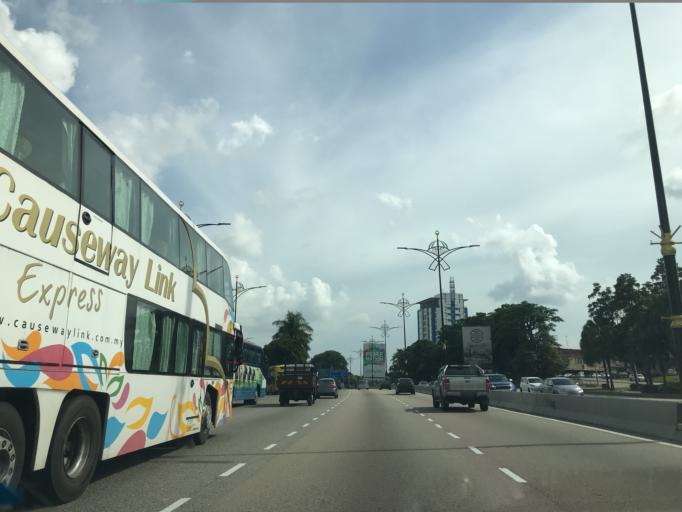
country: MY
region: Johor
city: Skudai
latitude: 1.5444
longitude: 103.6577
